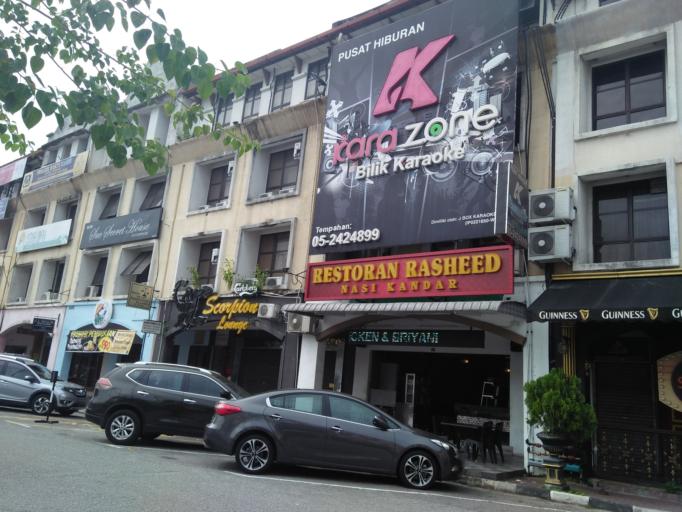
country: MY
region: Perak
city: Ipoh
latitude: 4.5993
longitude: 101.0950
